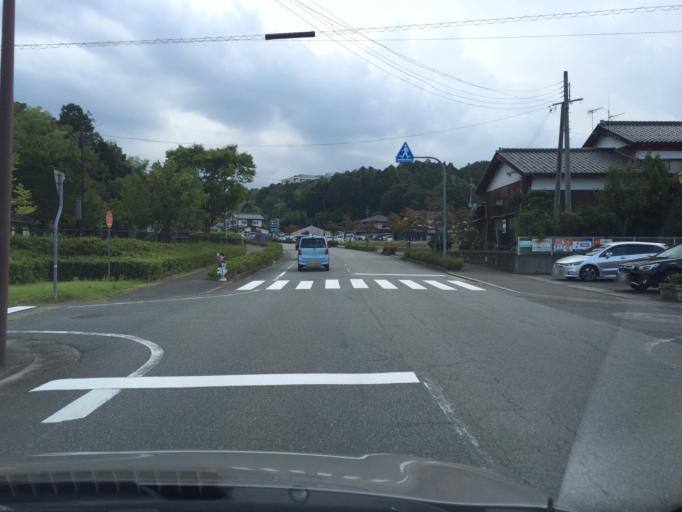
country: JP
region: Hyogo
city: Toyooka
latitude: 35.5323
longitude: 134.8079
